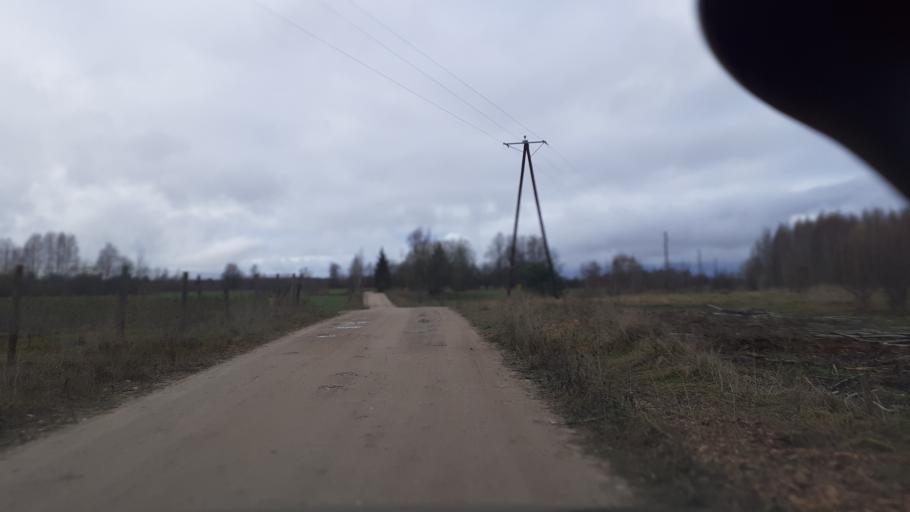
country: LV
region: Kuldigas Rajons
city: Kuldiga
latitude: 57.0421
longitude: 21.8759
